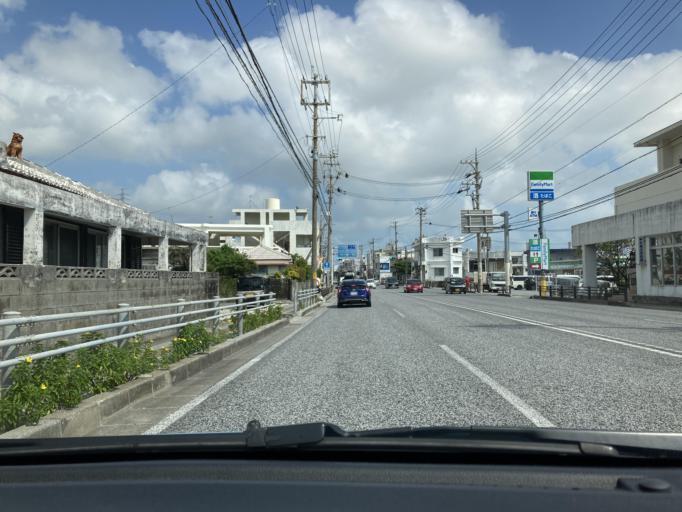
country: JP
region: Okinawa
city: Okinawa
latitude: 26.3234
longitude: 127.8221
